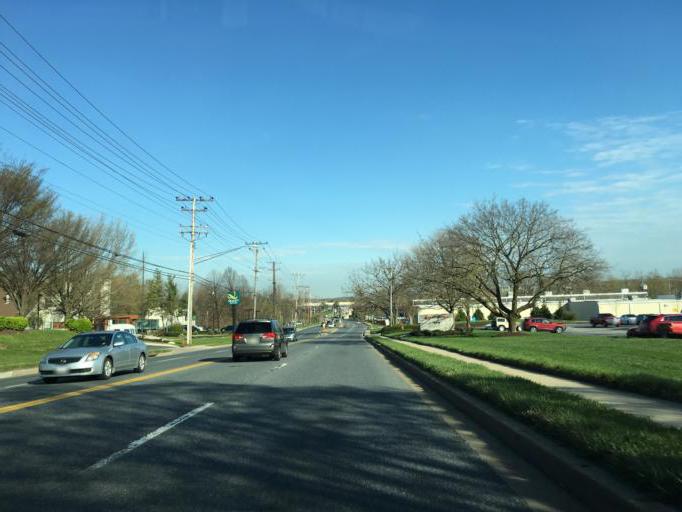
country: US
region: Maryland
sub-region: Baltimore County
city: Cockeysville
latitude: 39.4774
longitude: -76.6526
